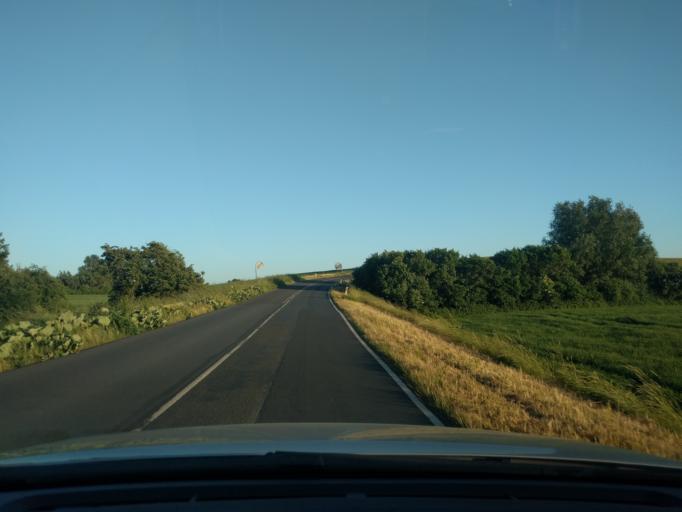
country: DK
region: South Denmark
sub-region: Kerteminde Kommune
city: Kerteminde
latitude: 55.5702
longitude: 10.6471
